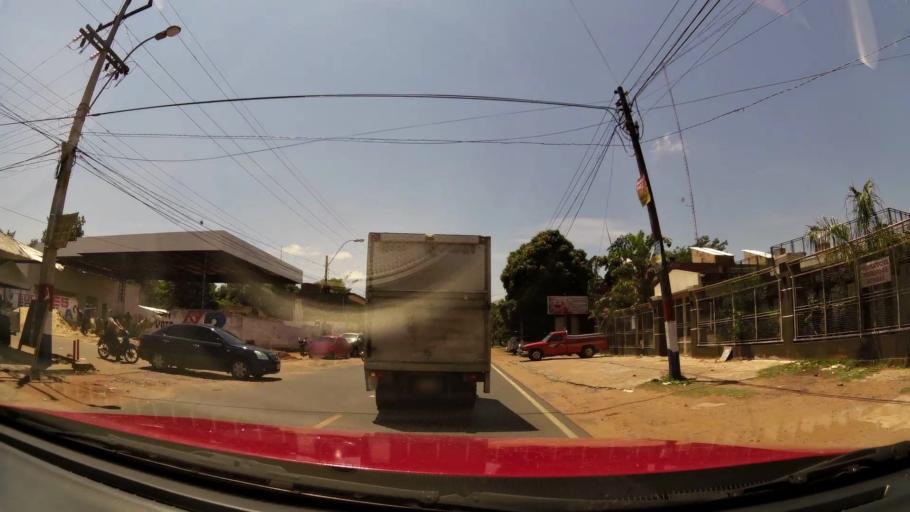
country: PY
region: Central
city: San Antonio
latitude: -25.4111
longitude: -57.5490
